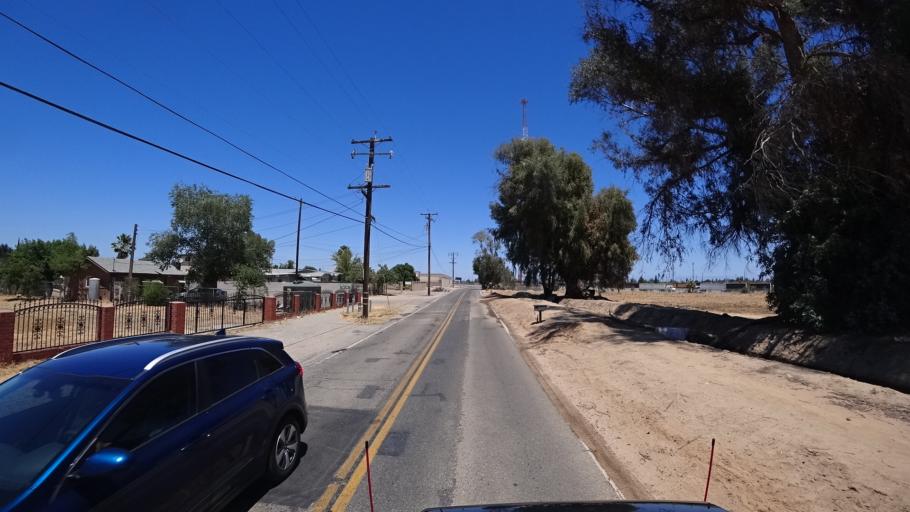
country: US
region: California
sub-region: Fresno County
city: West Park
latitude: 36.7828
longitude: -119.8534
